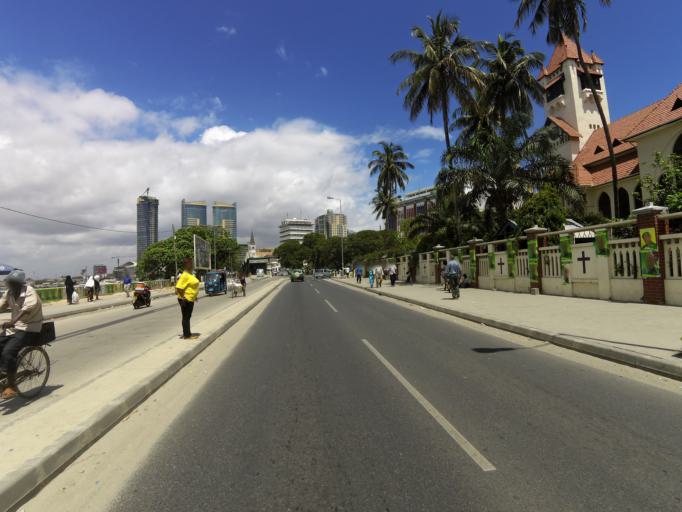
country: TZ
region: Dar es Salaam
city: Dar es Salaam
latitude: -6.8179
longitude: 39.2915
